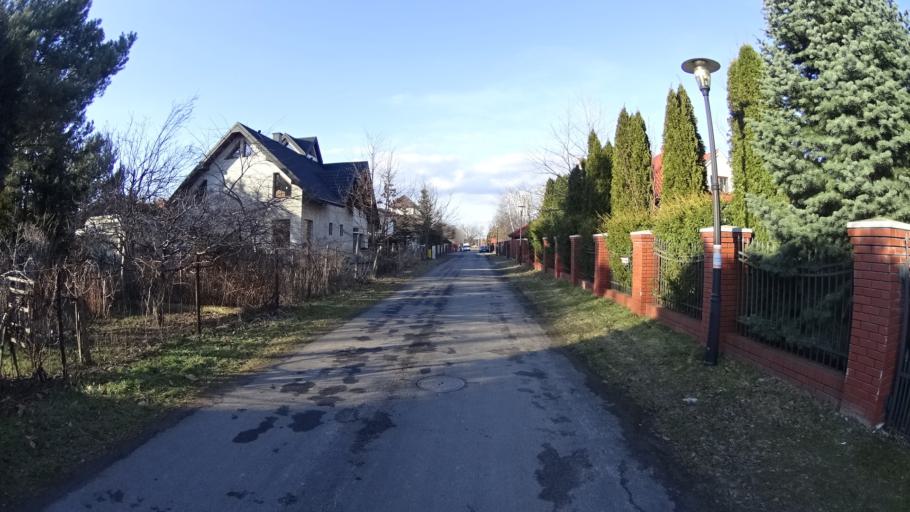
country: PL
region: Masovian Voivodeship
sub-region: Powiat warszawski zachodni
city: Hornowek
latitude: 52.2626
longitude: 20.7920
